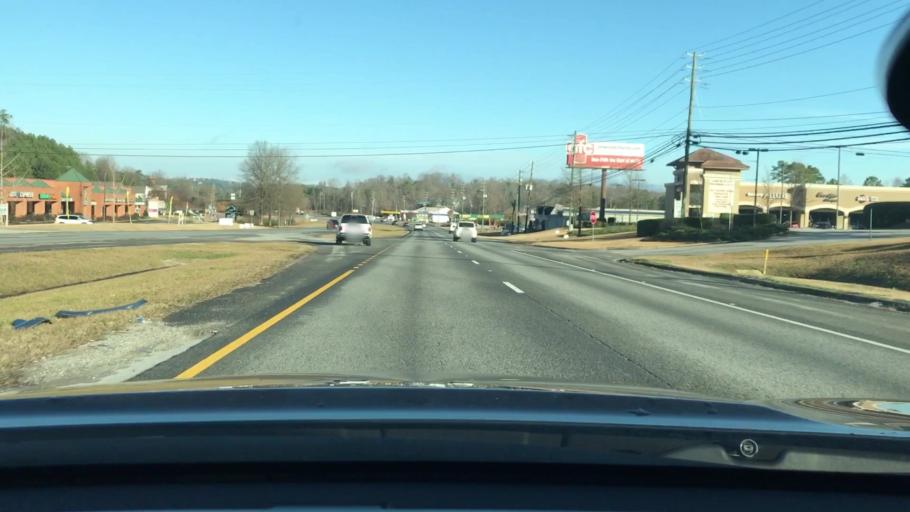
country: US
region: Alabama
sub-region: Shelby County
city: Lake Purdy
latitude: 33.4106
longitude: -86.6645
